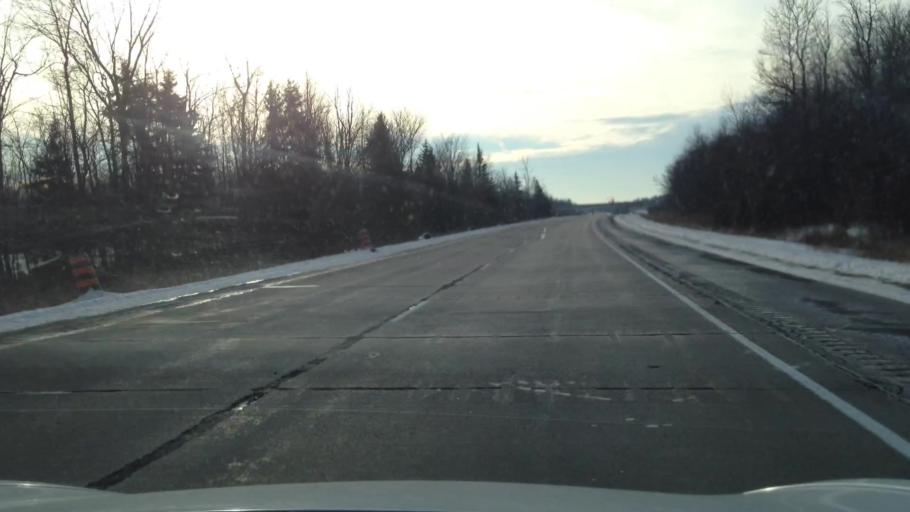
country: CA
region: Ontario
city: Hawkesbury
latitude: 45.4971
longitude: -74.6071
